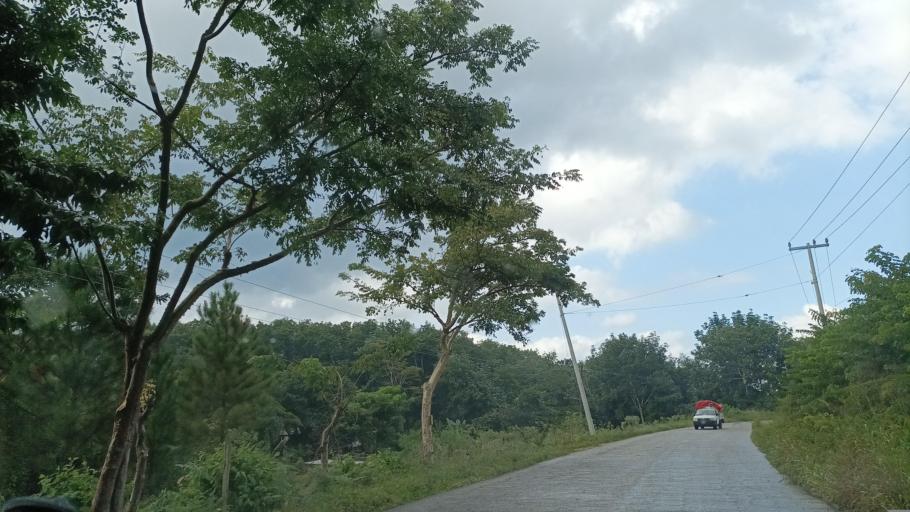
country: MX
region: Veracruz
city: Las Choapas
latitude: 17.8490
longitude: -94.1062
